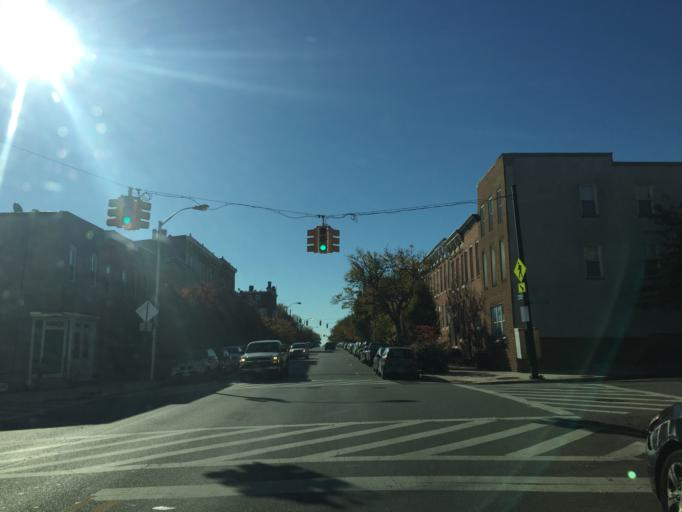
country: US
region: Maryland
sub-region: City of Baltimore
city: Baltimore
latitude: 39.2932
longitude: -76.5848
